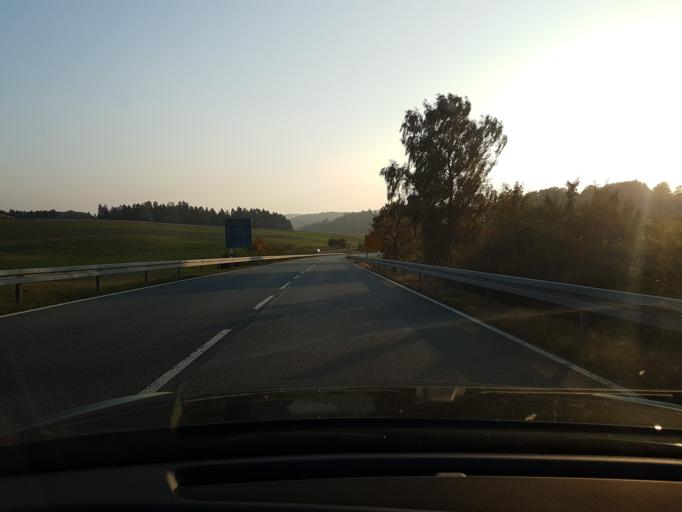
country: DE
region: Hesse
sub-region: Regierungsbezirk Darmstadt
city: Beerfelden
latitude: 49.5574
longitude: 8.9810
